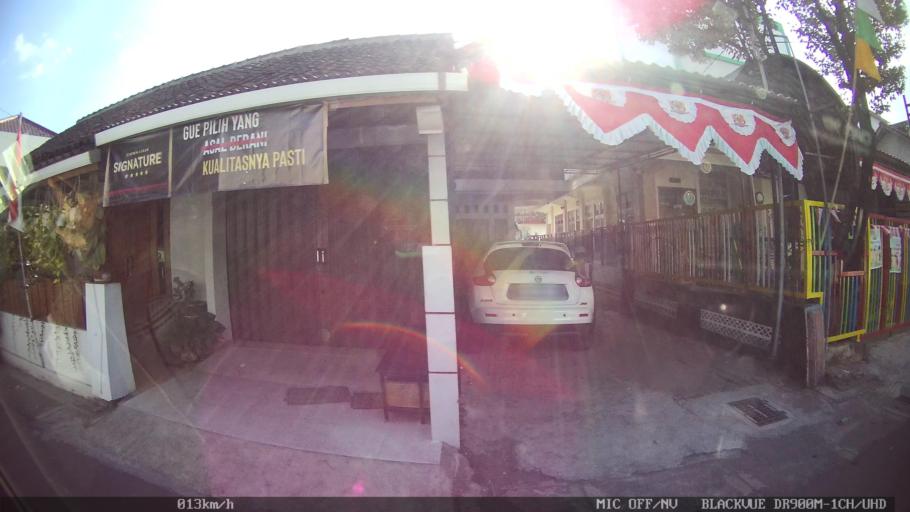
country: ID
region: Daerah Istimewa Yogyakarta
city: Yogyakarta
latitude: -7.7972
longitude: 110.3507
